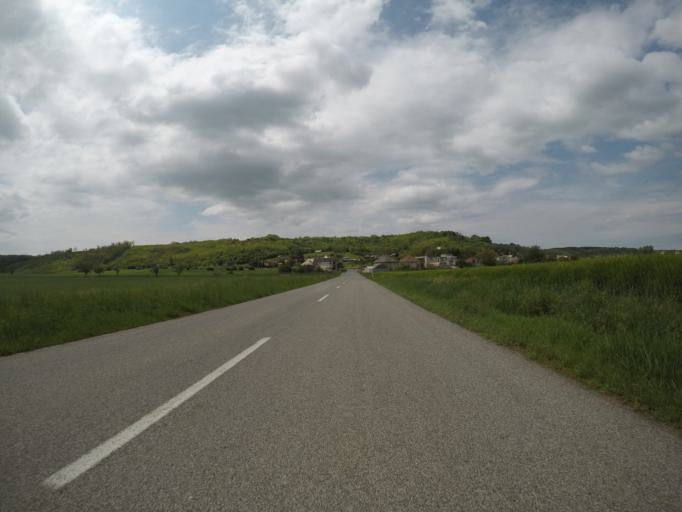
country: SK
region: Banskobystricky
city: Dudince
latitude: 48.0821
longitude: 18.8049
